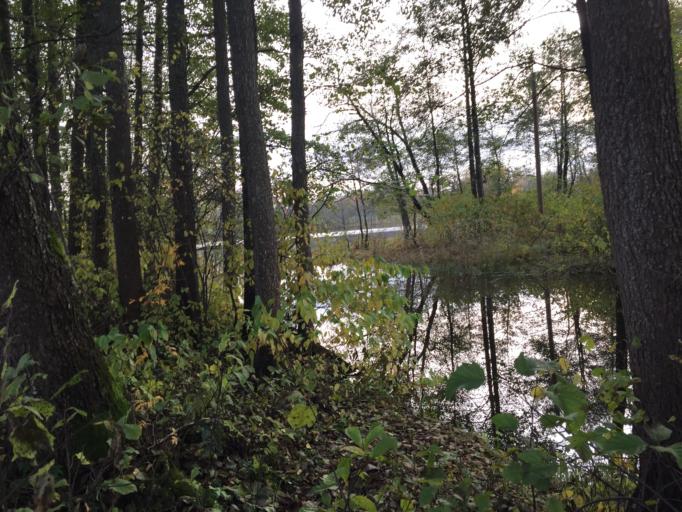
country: LV
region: Cesu Rajons
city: Cesis
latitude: 57.3223
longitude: 25.1498
